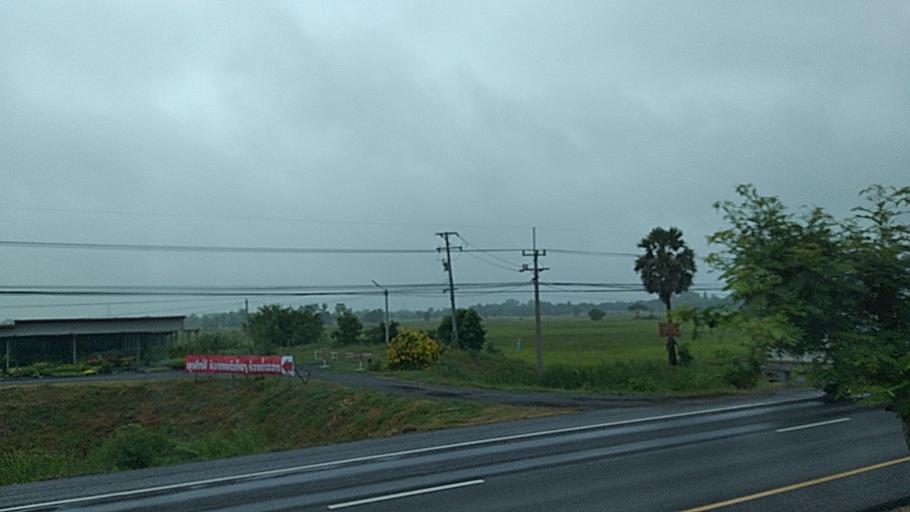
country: TH
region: Nakhon Ratchasima
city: Phimai
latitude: 15.3055
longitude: 102.4236
